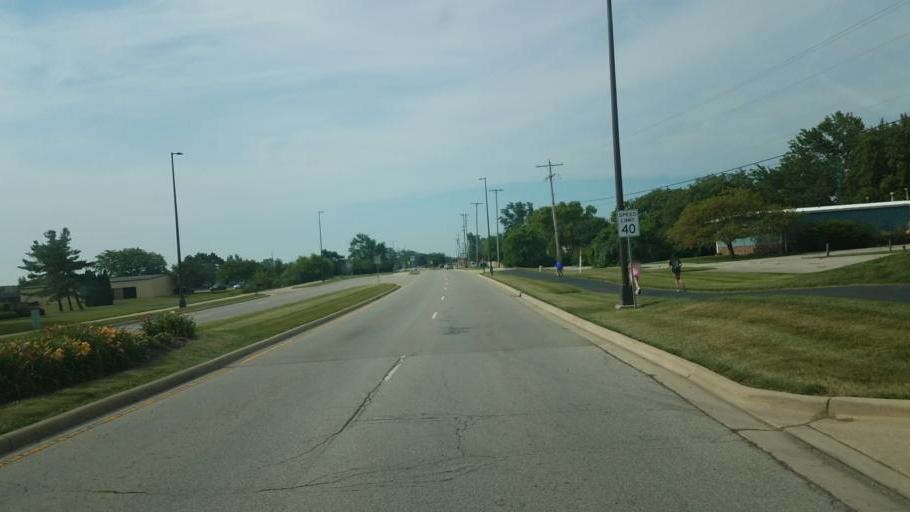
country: US
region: Ohio
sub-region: Franklin County
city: Dublin
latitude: 40.0948
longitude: -83.1587
